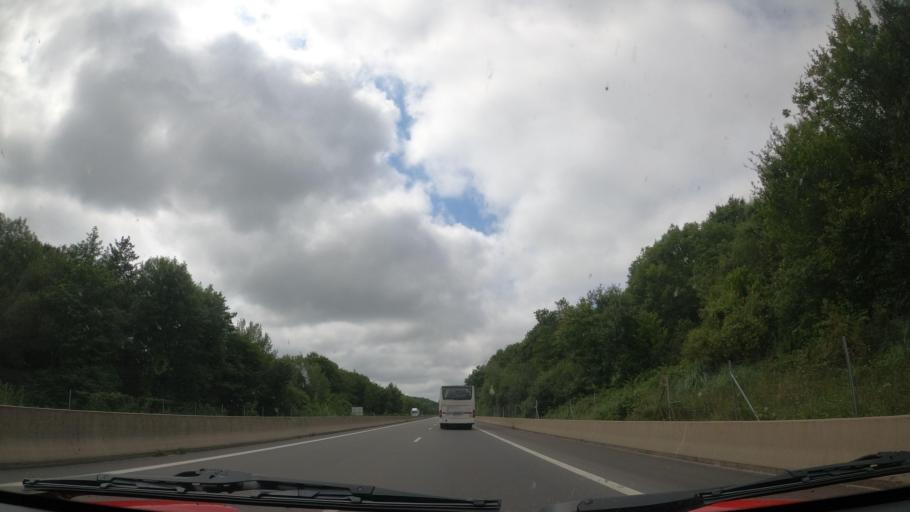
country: FR
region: Aquitaine
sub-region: Departement des Pyrenees-Atlantiques
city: Mouguerre
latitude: 43.4556
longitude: -1.4068
